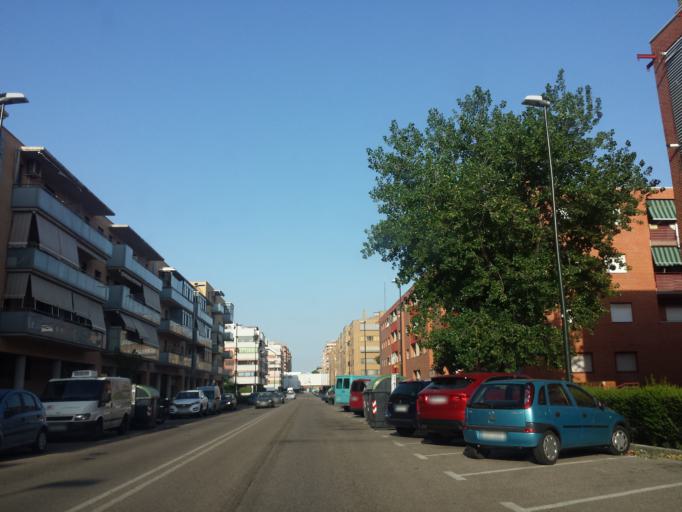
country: ES
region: Aragon
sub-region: Provincia de Zaragoza
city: Almozara
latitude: 41.6761
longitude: -0.8951
